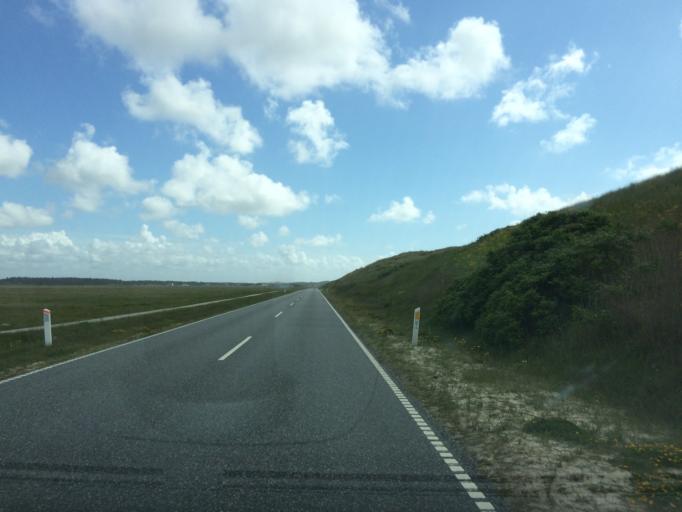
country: DK
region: Central Jutland
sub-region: Holstebro Kommune
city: Ulfborg
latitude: 56.3345
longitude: 8.1228
